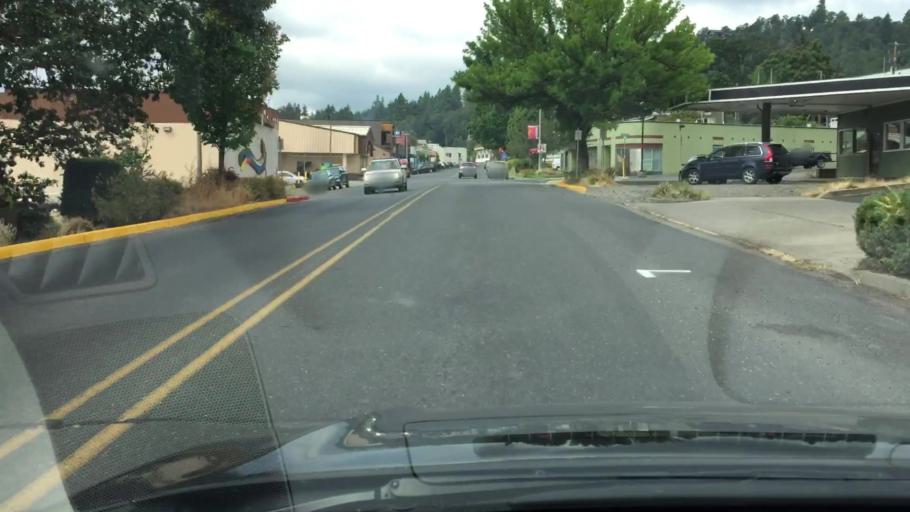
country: US
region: Washington
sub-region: Klickitat County
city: White Salmon
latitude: 45.7270
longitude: -121.4833
